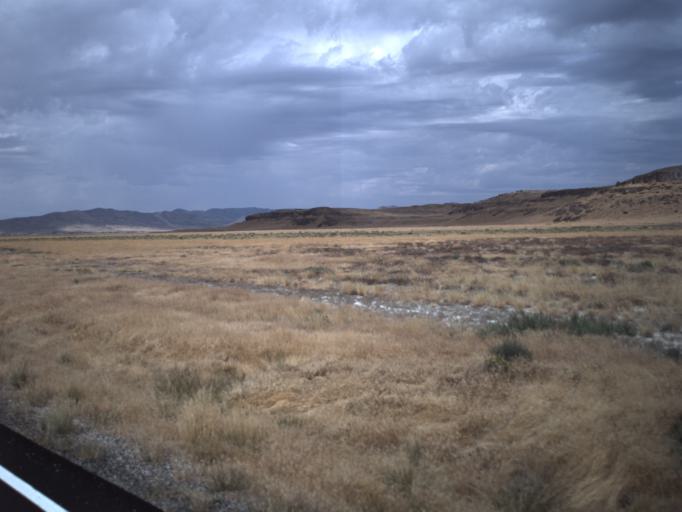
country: US
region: Utah
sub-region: Tooele County
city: Wendover
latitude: 41.4214
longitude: -113.8907
